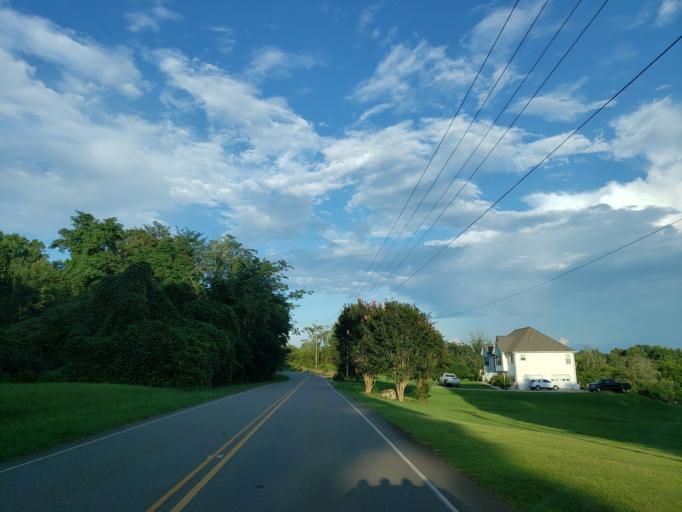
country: US
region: Georgia
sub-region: Cherokee County
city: Canton
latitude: 34.3279
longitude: -84.4793
